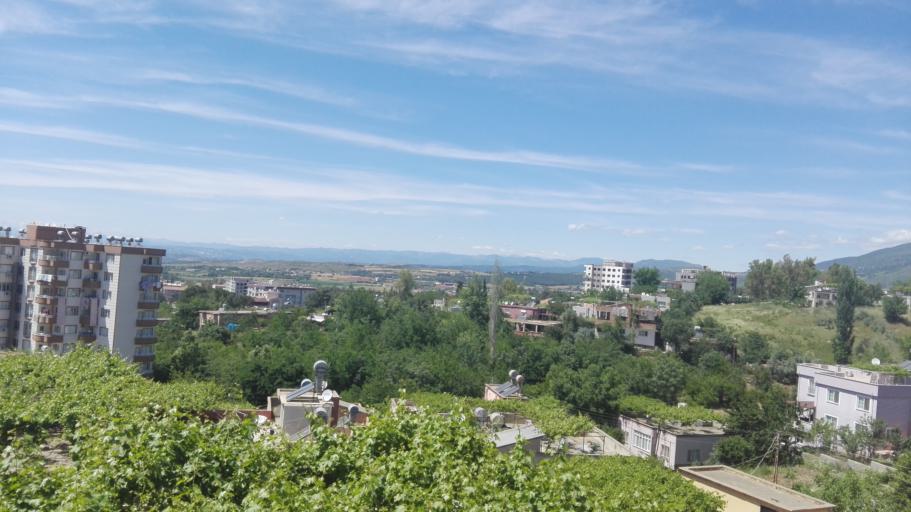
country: TR
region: Osmaniye
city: Haruniye
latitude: 37.2499
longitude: 36.4677
